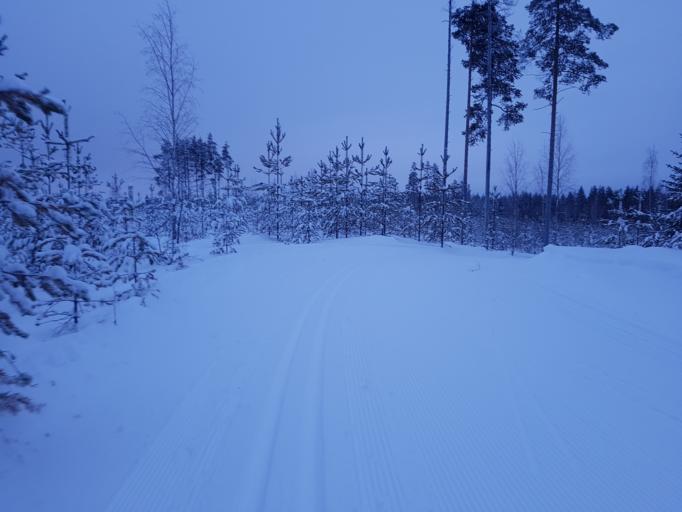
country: FI
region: Kainuu
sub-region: Kehys-Kainuu
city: Kuhmo
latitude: 64.0871
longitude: 29.5167
